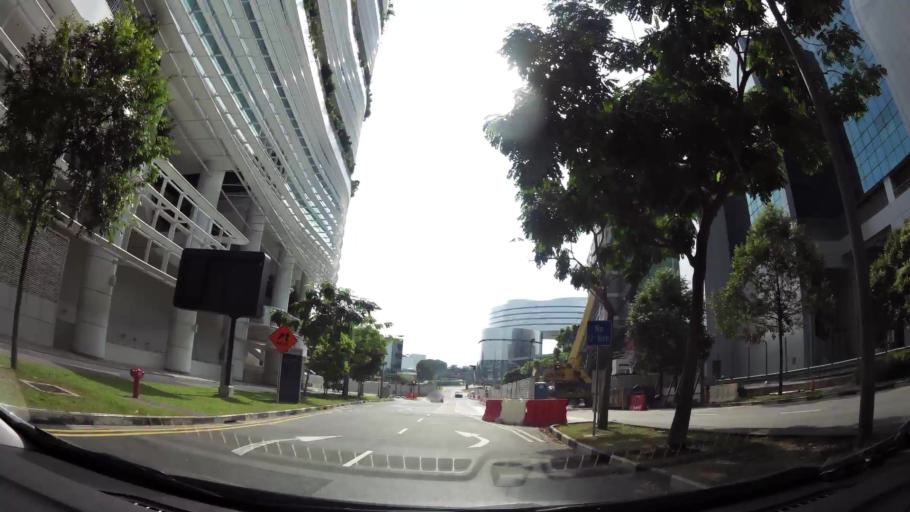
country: SG
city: Singapore
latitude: 1.2976
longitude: 103.7896
